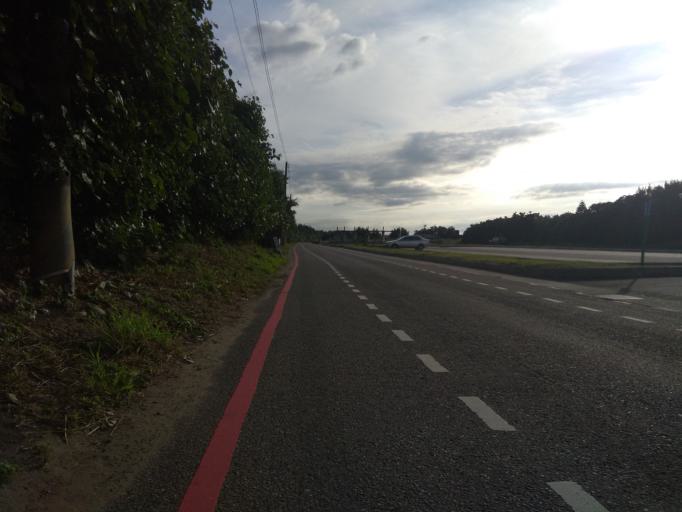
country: TW
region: Taiwan
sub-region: Hsinchu
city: Zhubei
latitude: 24.9786
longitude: 121.0160
